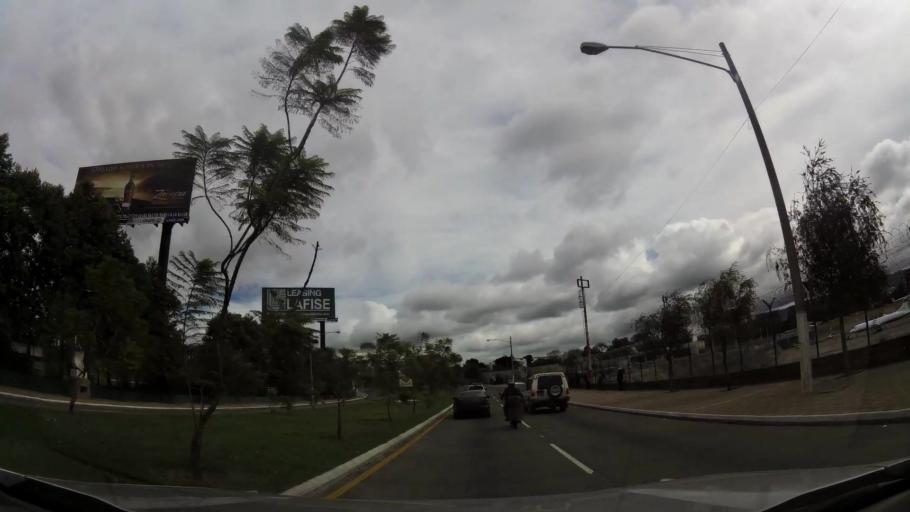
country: GT
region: Guatemala
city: Santa Catarina Pinula
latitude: 14.5934
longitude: -90.5286
